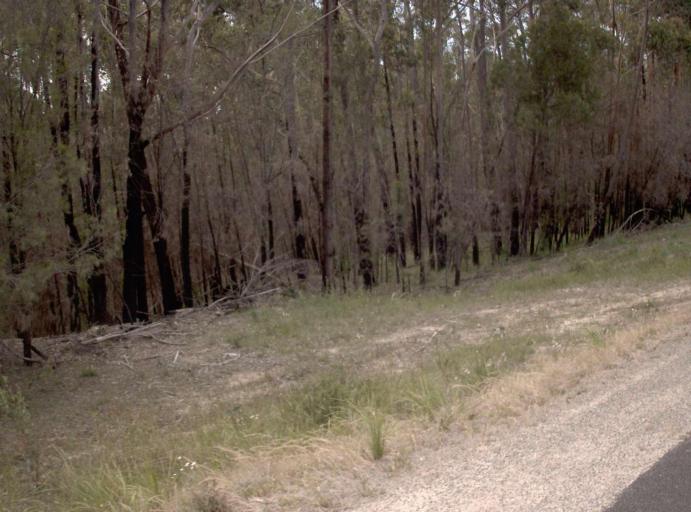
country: AU
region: New South Wales
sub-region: Bega Valley
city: Eden
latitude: -37.5396
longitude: 149.4646
